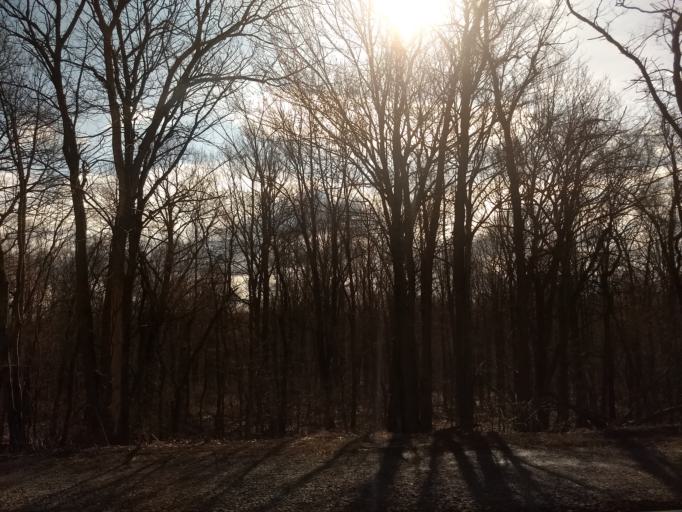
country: US
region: Pennsylvania
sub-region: Blair County
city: Duncansville
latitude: 40.4777
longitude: -78.4778
